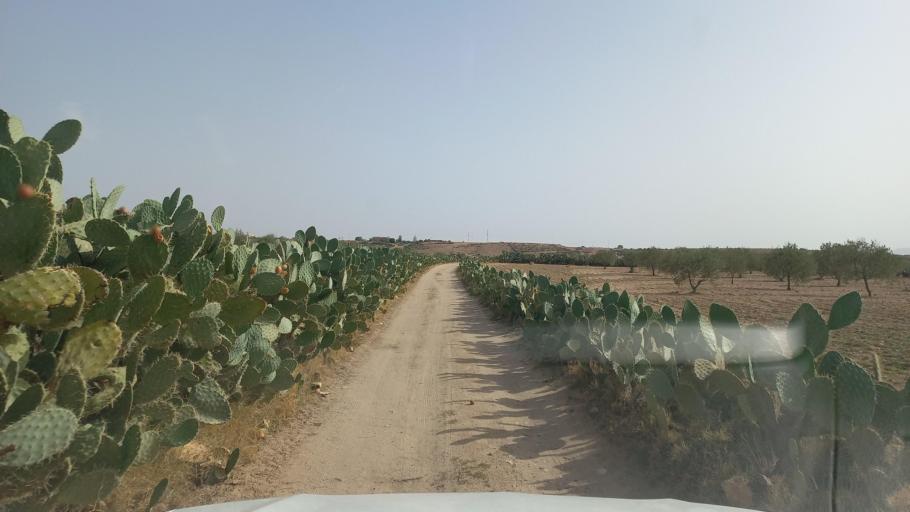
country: TN
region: Al Qasrayn
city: Kasserine
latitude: 35.2971
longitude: 8.9623
